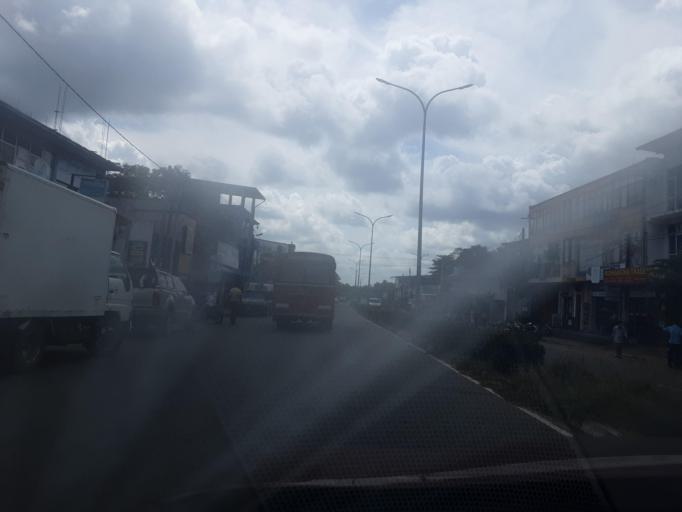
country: LK
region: North Western
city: Kuliyapitiya
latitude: 7.4707
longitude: 80.0253
